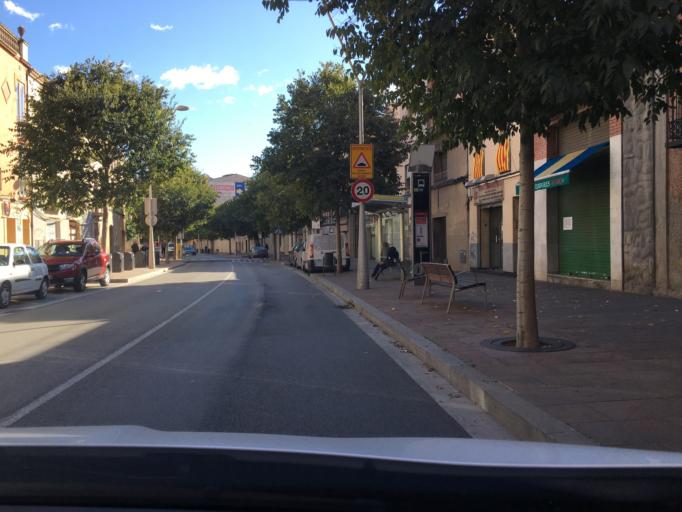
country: ES
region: Catalonia
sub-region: Provincia de Barcelona
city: Sant Feliu de Llobregat
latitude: 41.3832
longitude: 2.0419
